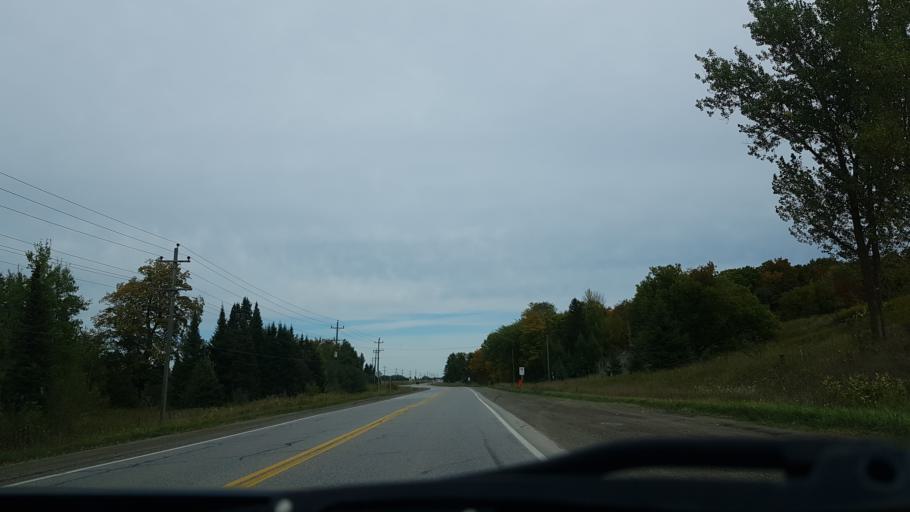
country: CA
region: Ontario
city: Orangeville
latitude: 43.8139
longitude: -80.0466
